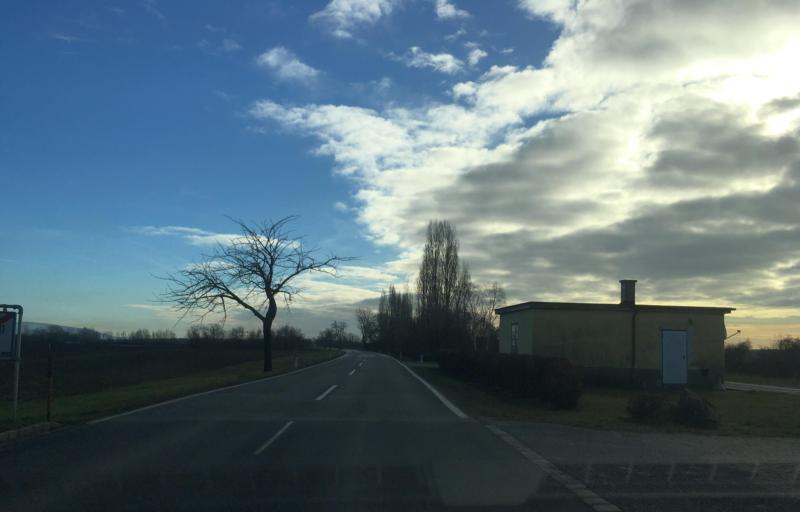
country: AT
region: Lower Austria
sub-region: Politischer Bezirk Ganserndorf
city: Eckartsau
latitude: 48.1608
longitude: 16.7598
